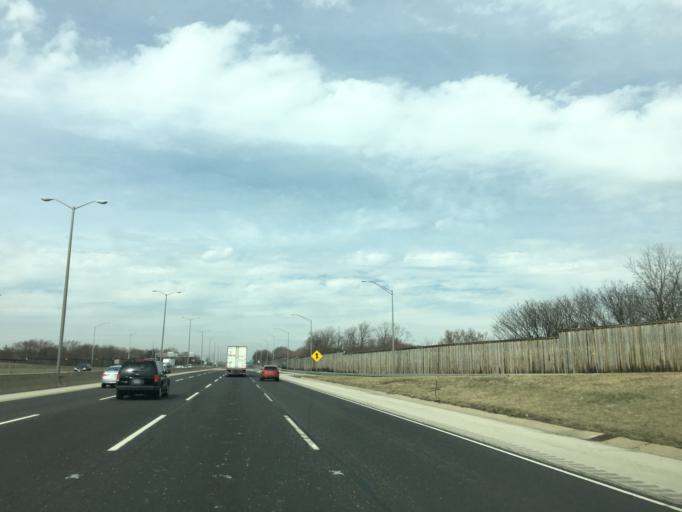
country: US
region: Illinois
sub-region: DuPage County
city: Woodridge
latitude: 41.7732
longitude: -88.0464
